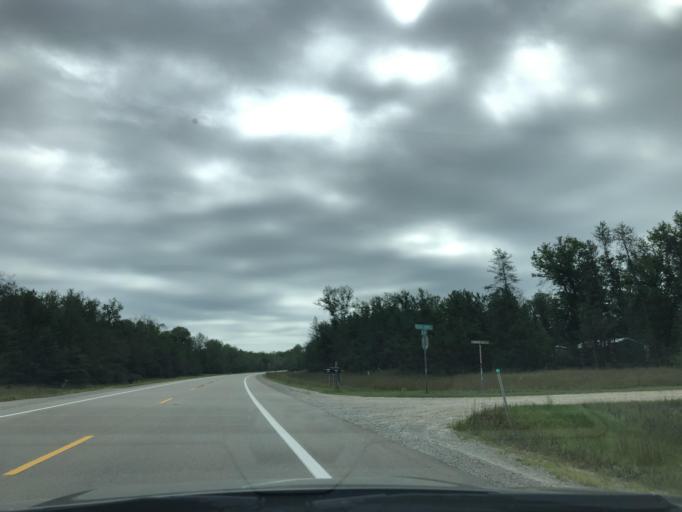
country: US
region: Michigan
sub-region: Clare County
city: Harrison
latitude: 44.0427
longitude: -85.0434
